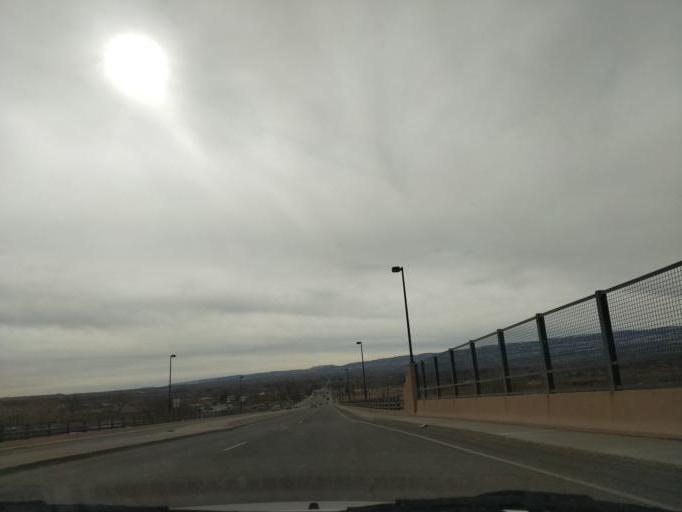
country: US
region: Colorado
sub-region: Mesa County
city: Fruitvale
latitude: 39.0718
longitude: -108.5153
